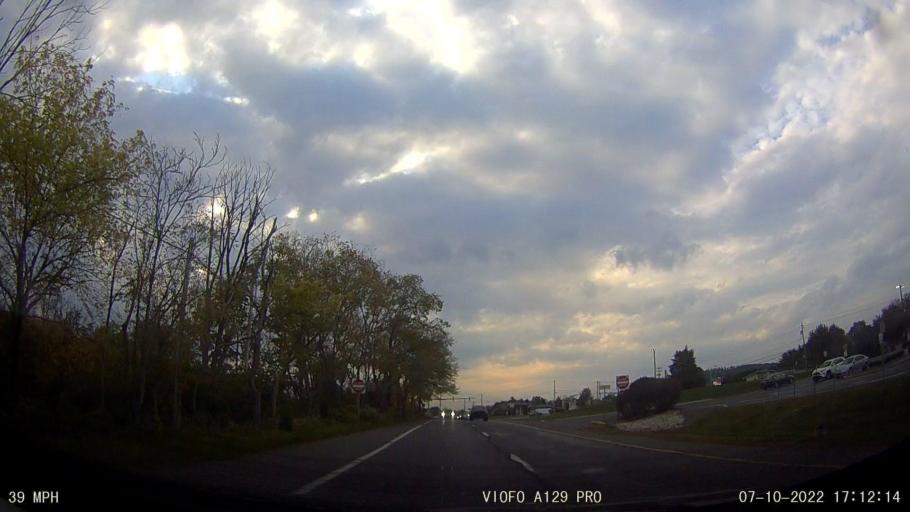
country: US
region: Pennsylvania
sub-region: Berks County
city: Amity Gardens
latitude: 40.2633
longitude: -75.7414
